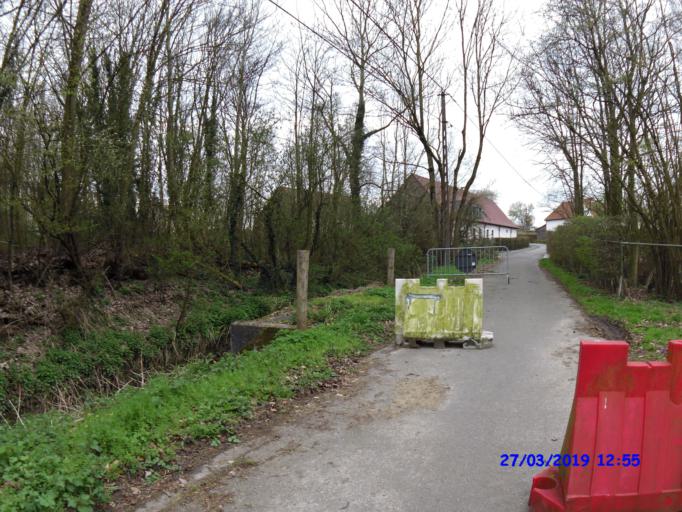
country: BE
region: Flanders
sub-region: Provincie Vlaams-Brabant
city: Ternat
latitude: 50.8714
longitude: 4.1963
